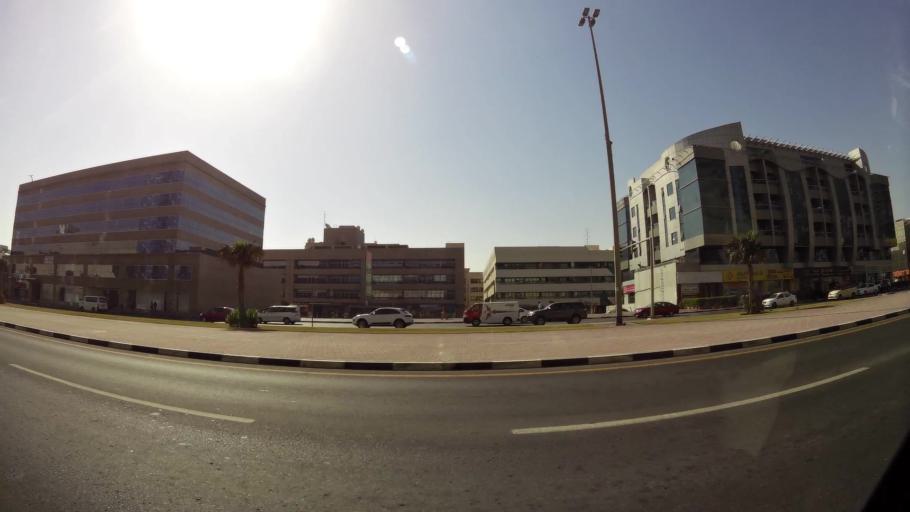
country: AE
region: Ash Shariqah
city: Sharjah
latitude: 25.2515
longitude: 55.3024
